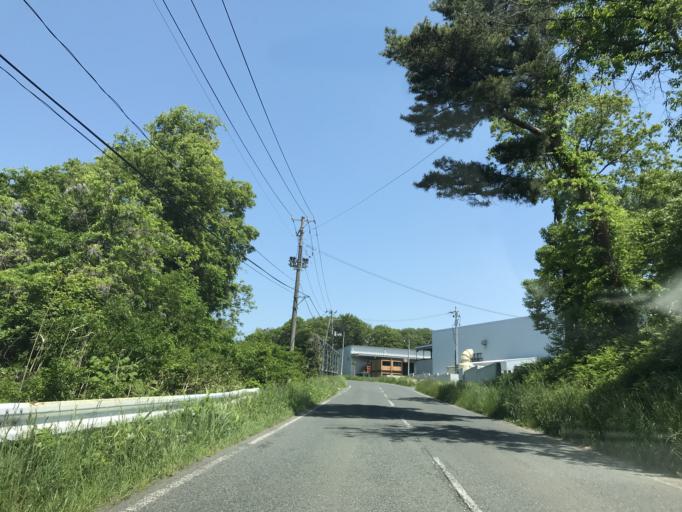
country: JP
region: Iwate
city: Kitakami
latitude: 39.2083
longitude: 141.0665
